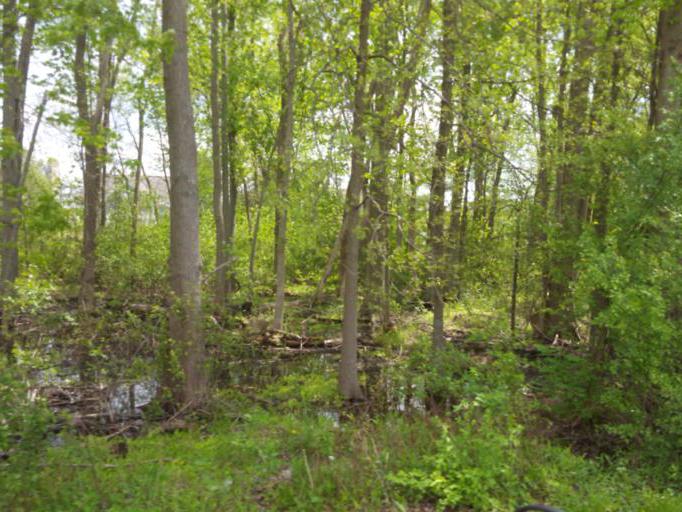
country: US
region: Ohio
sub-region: Perry County
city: Thornport
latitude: 39.9199
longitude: -82.4272
